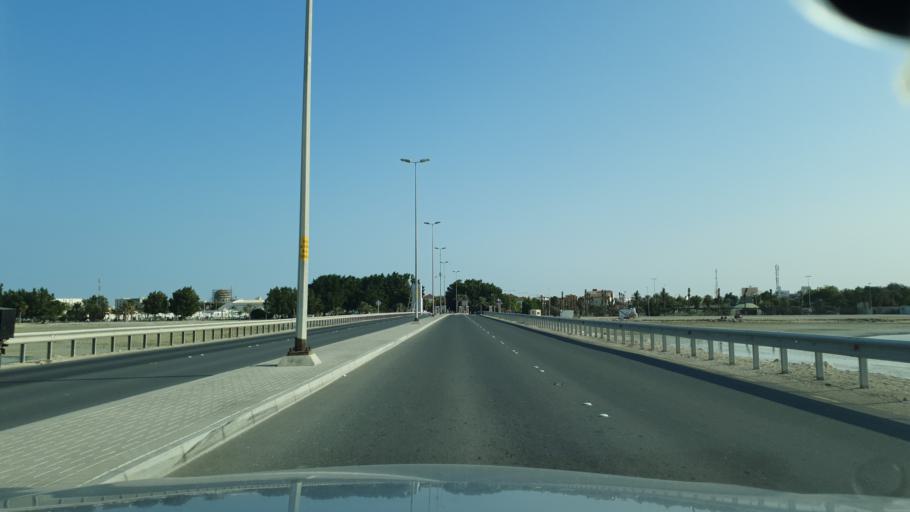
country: BH
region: Manama
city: Jidd Hafs
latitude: 26.2260
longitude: 50.4578
